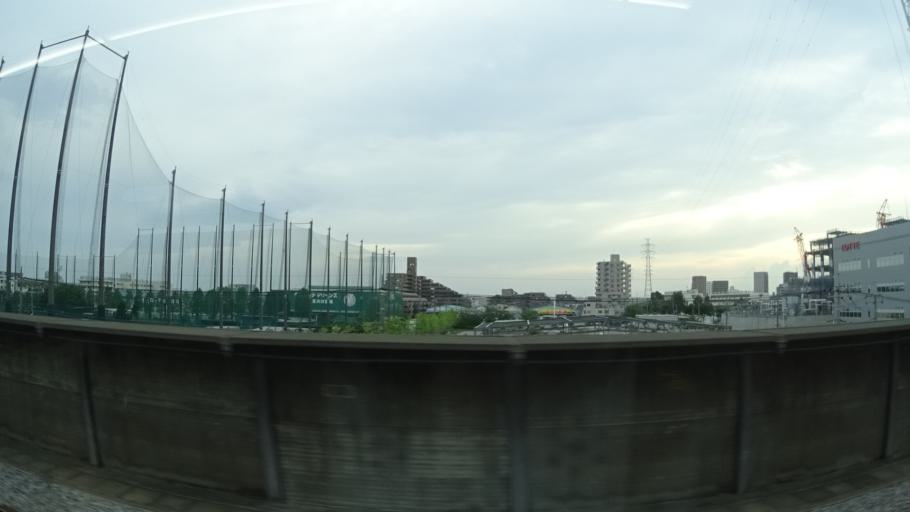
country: JP
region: Saitama
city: Shimotoda
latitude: 35.8392
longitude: 139.6503
